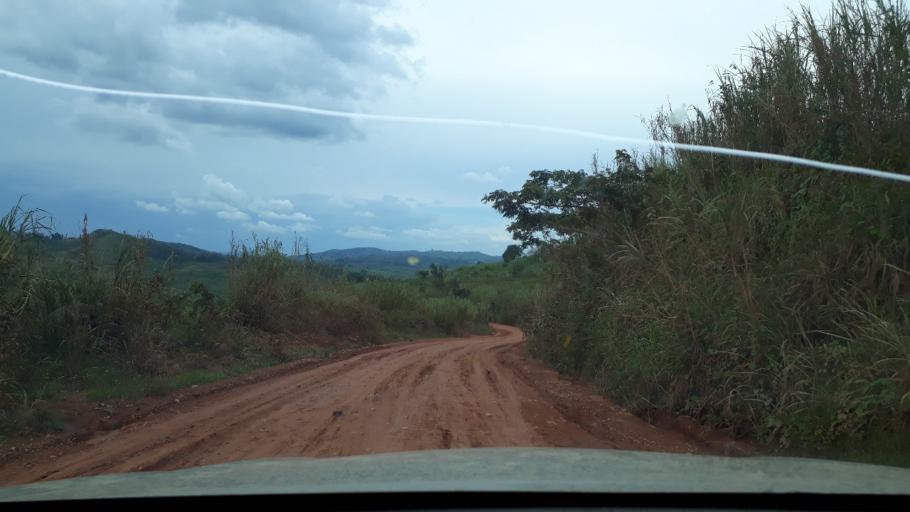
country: CD
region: Eastern Province
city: Bunia
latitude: 1.7615
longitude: 30.3828
